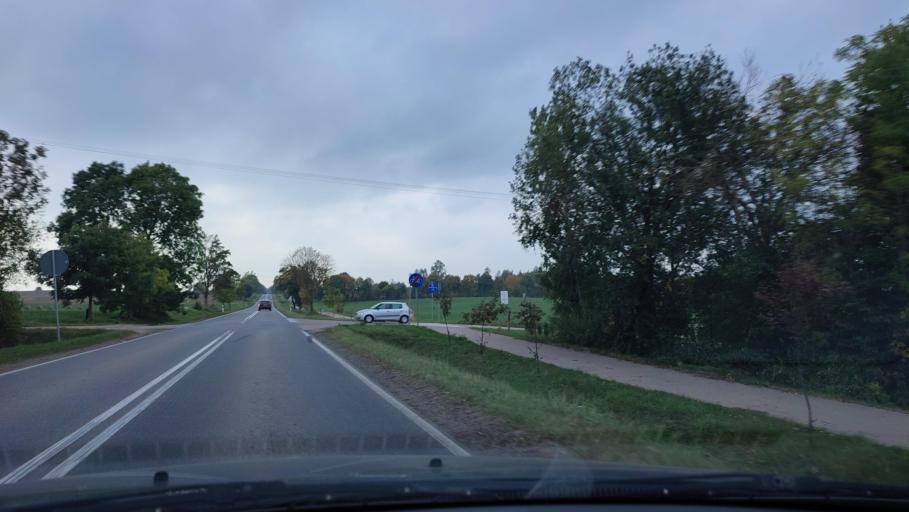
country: PL
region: Warmian-Masurian Voivodeship
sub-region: Powiat nidzicki
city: Nidzica
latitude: 53.3546
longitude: 20.3819
